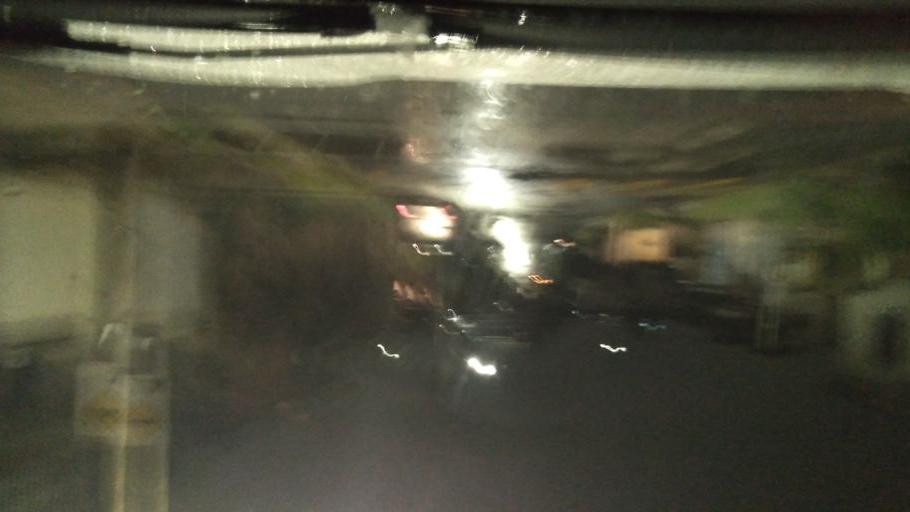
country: BR
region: Minas Gerais
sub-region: Belo Horizonte
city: Belo Horizonte
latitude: -19.9001
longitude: -43.9595
